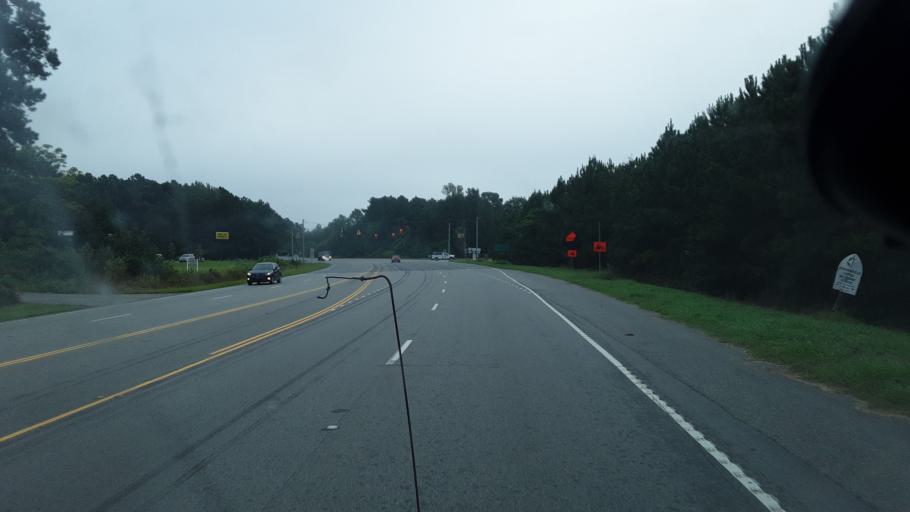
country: US
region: South Carolina
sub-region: Florence County
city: Johnsonville
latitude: 33.8820
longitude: -79.4547
